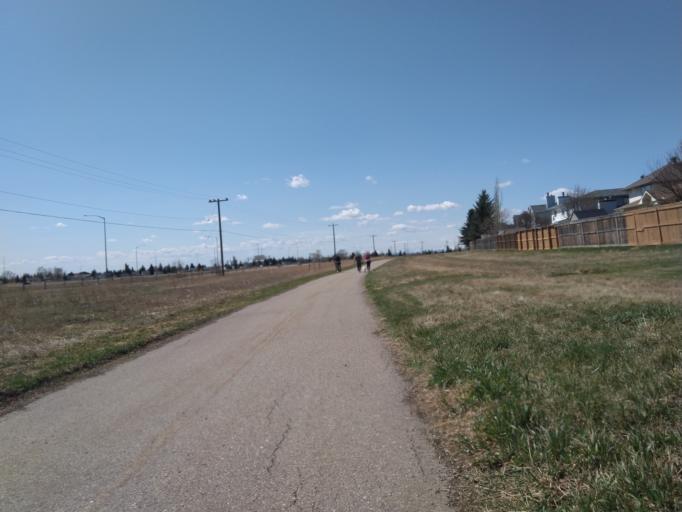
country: CA
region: Alberta
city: Chestermere
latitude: 51.0702
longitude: -113.9244
